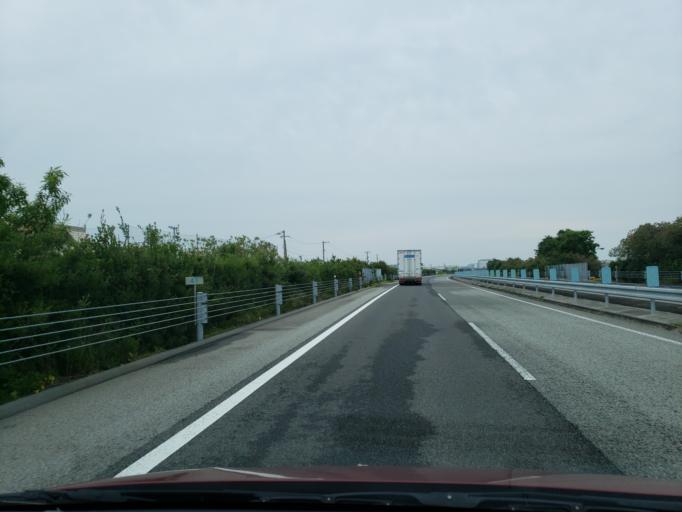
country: JP
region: Tokushima
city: Tokushima-shi
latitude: 34.1083
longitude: 134.5319
